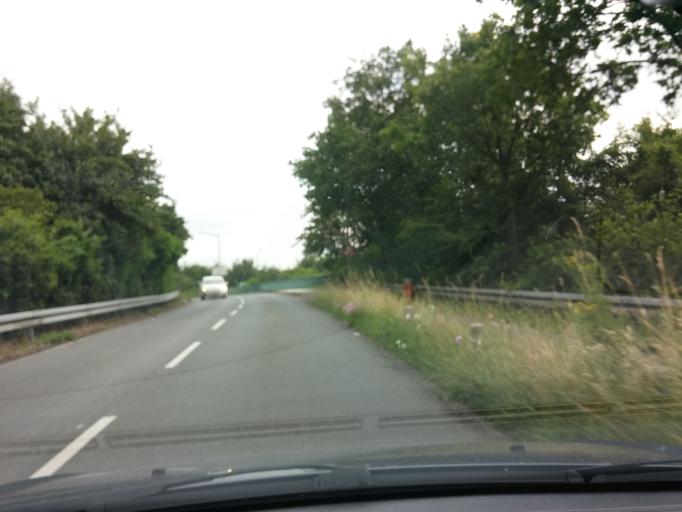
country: DE
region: North Rhine-Westphalia
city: Dorsten
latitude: 51.6169
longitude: 6.9715
